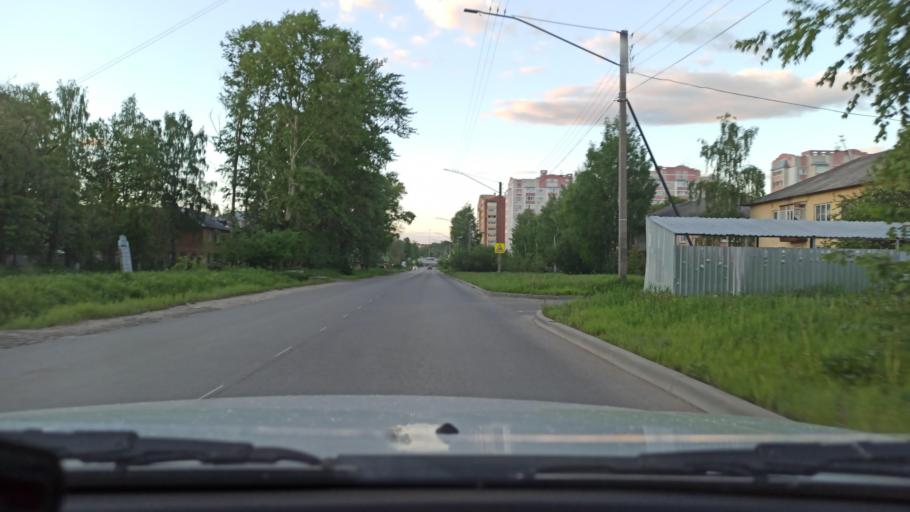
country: RU
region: Vologda
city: Vologda
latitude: 59.2174
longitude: 39.8502
